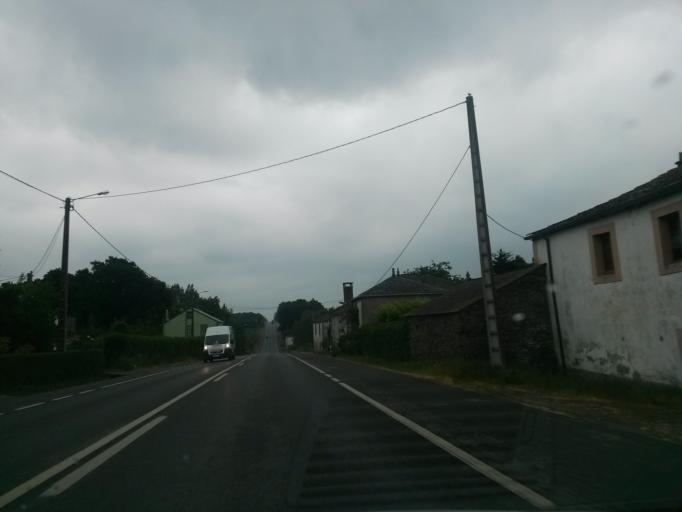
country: ES
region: Galicia
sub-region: Provincia de Lugo
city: Begonte
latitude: 43.1363
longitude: -7.6608
